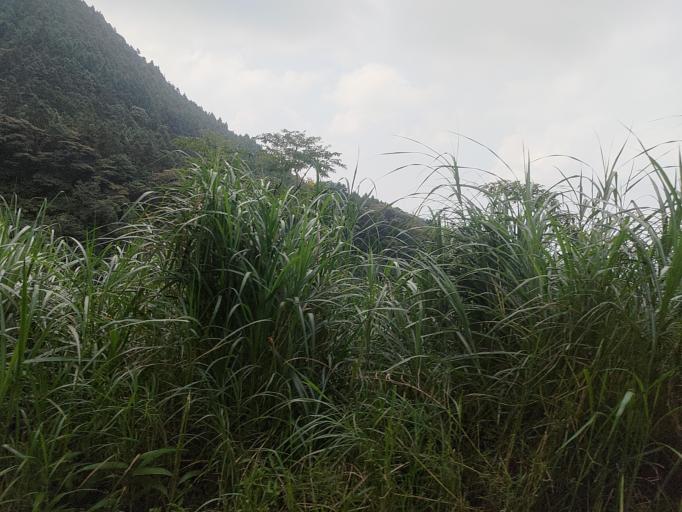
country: TW
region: Taiwan
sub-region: Hsinchu
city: Hsinchu
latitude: 24.6252
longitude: 121.0820
